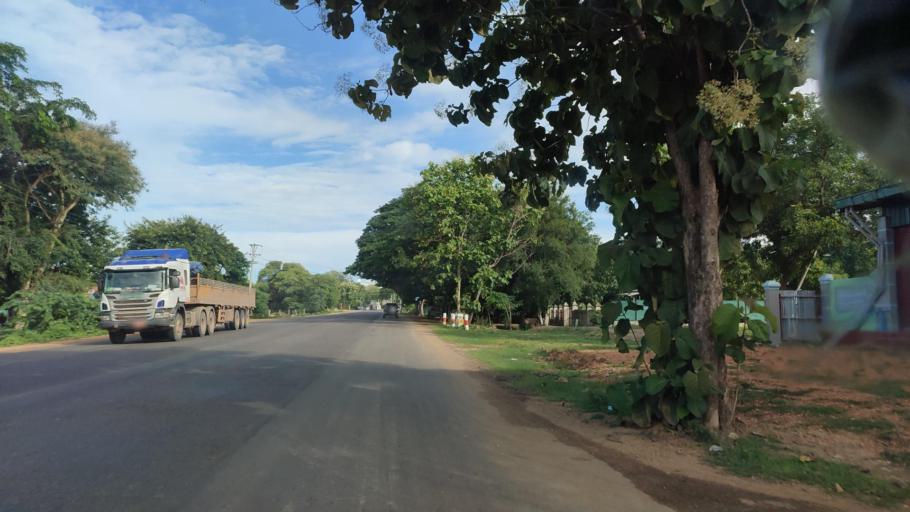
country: MM
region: Mandalay
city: Yamethin
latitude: 20.4483
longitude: 96.1301
